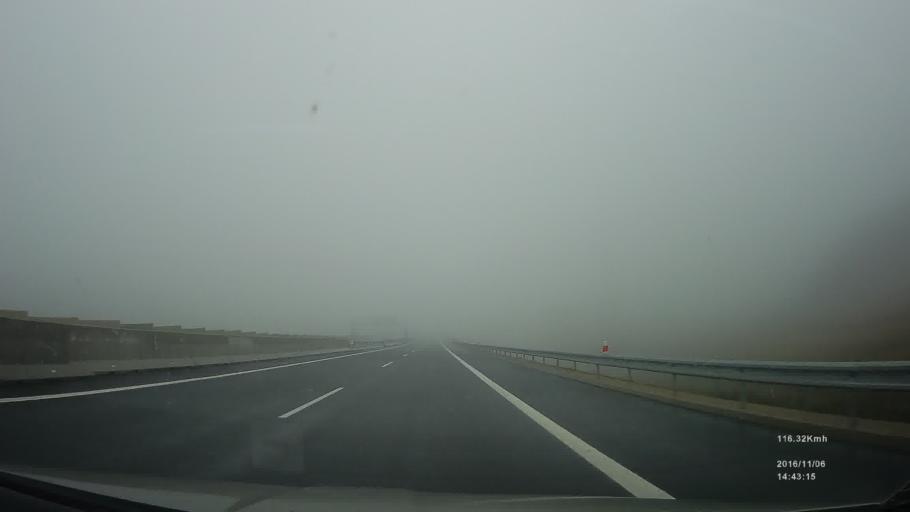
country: SK
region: Presovsky
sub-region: Okres Presov
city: Levoca
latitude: 49.0086
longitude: 20.6229
